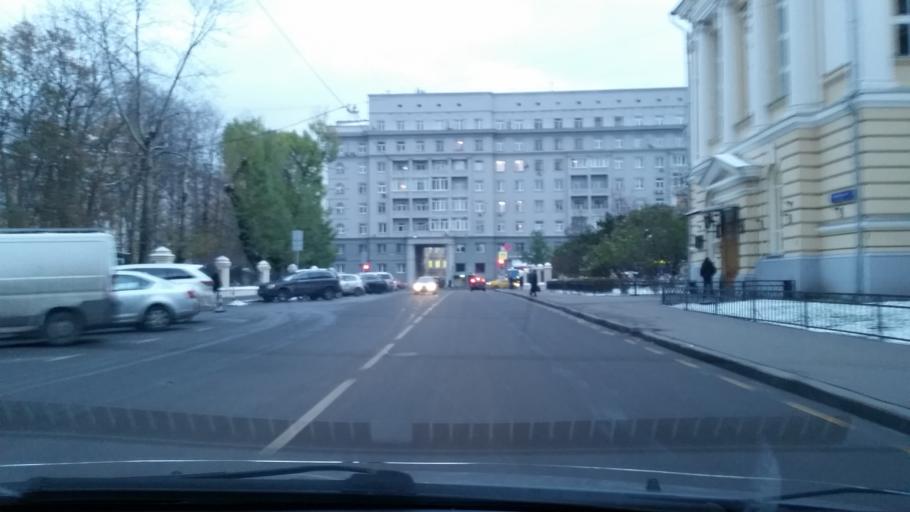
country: RU
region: Moscow
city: Luzhniki
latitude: 55.7299
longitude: 37.5636
